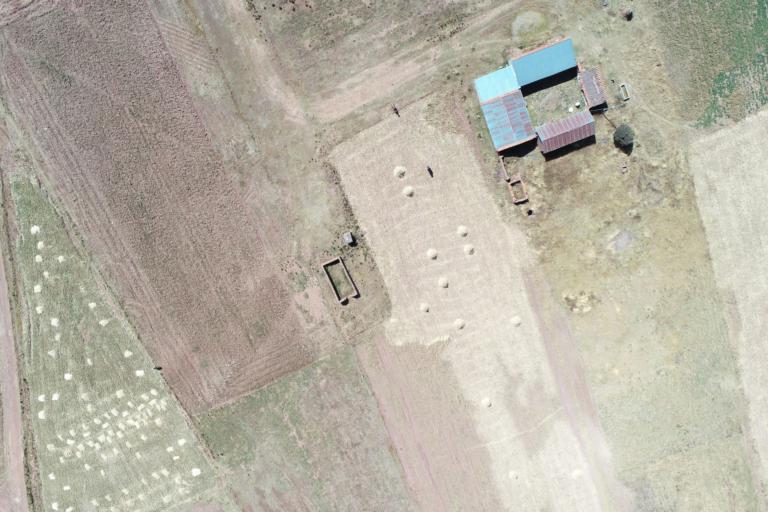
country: BO
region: La Paz
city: Tiahuanaco
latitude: -16.5899
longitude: -68.7702
